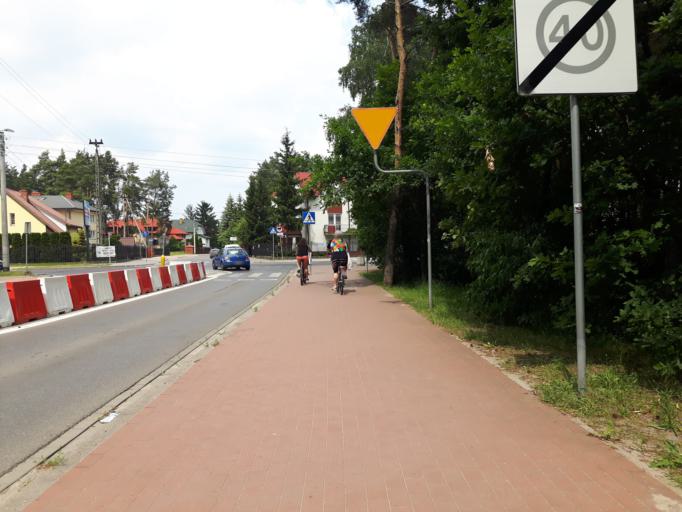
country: PL
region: Masovian Voivodeship
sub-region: Powiat wolominski
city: Zabki
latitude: 52.2904
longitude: 21.1257
